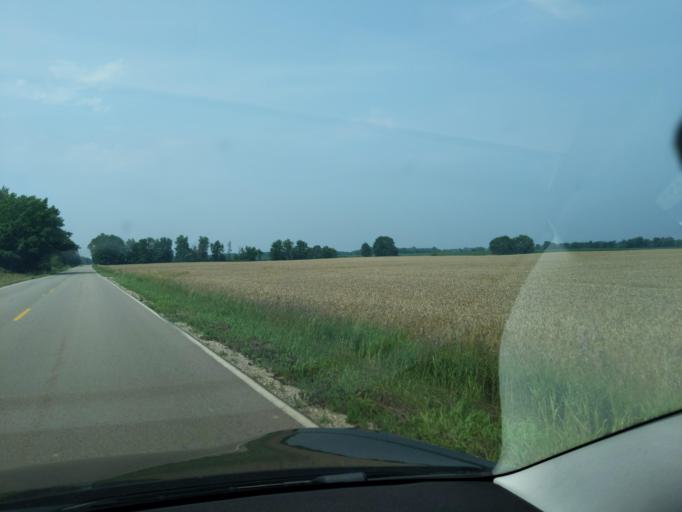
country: US
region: Michigan
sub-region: Clinton County
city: DeWitt
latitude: 42.9189
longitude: -84.5822
